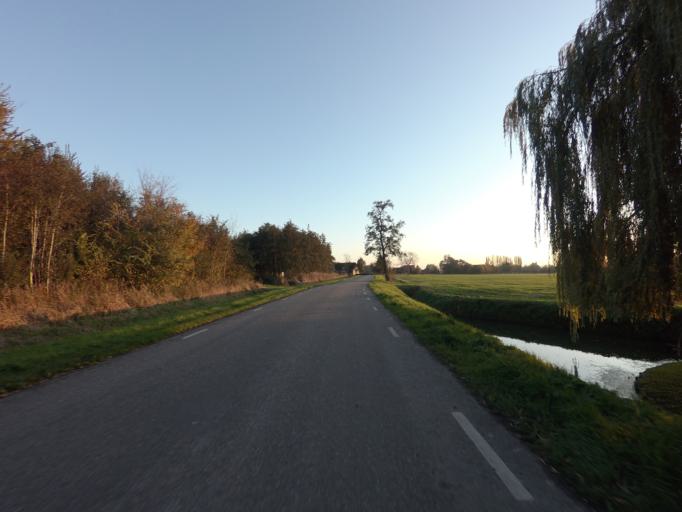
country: NL
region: North Brabant
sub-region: Gemeente Woudrichem
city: Woudrichem
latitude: 51.7908
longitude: 5.0117
